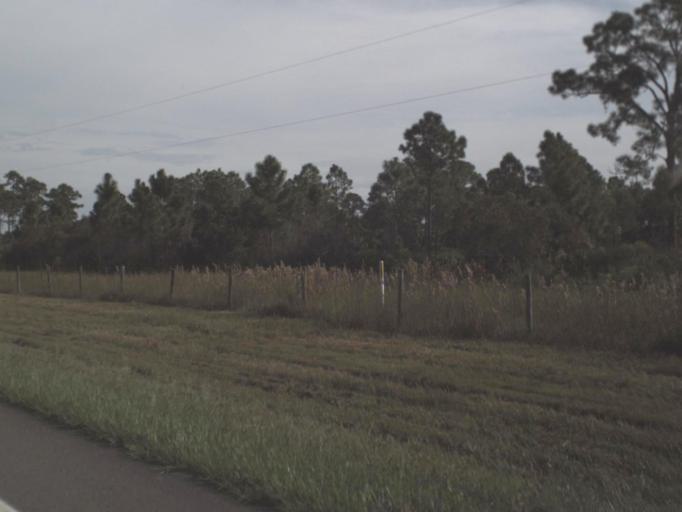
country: US
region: Florida
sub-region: Lee County
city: Olga
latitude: 26.8428
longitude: -81.7598
